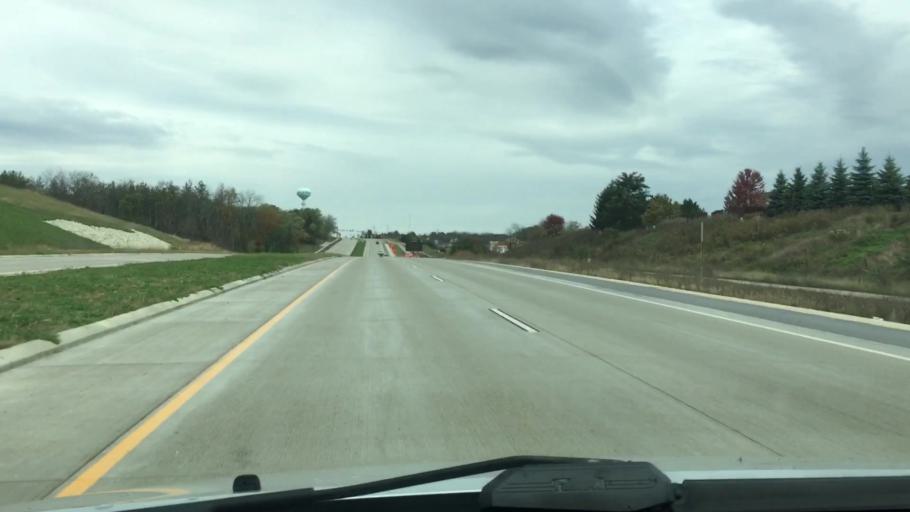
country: US
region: Wisconsin
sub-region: Waukesha County
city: Waukesha
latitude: 43.0291
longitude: -88.2857
